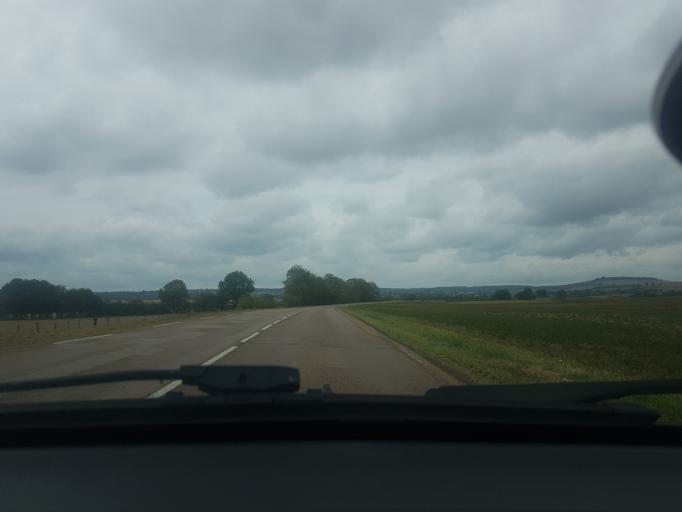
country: FR
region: Bourgogne
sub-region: Departement de la Cote-d'Or
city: Arnay-le-Duc
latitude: 47.1866
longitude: 4.3963
